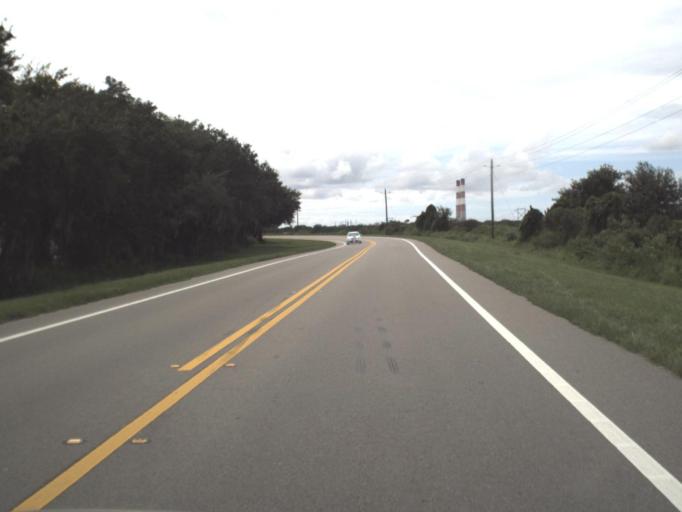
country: US
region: Florida
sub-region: Hillsborough County
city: Wimauma
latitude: 27.6023
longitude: -82.3162
